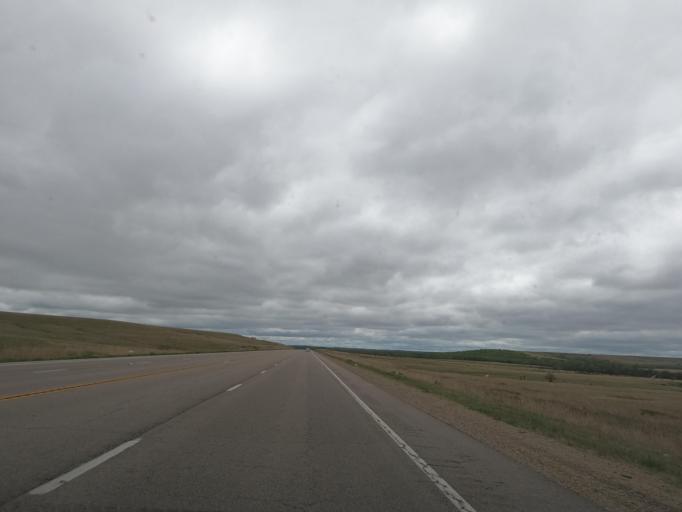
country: US
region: Kansas
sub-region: Greenwood County
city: Eureka
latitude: 37.6413
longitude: -96.4111
